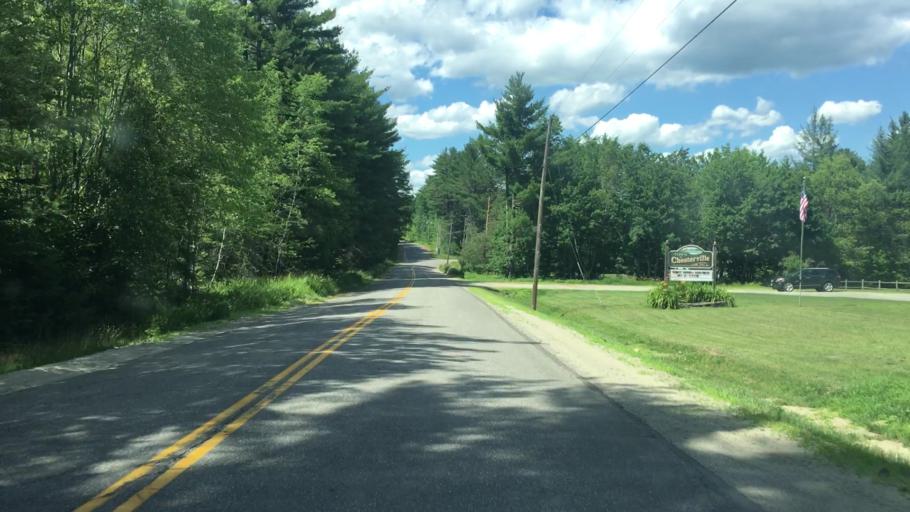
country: US
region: Maine
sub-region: Franklin County
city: Chesterville
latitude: 44.5786
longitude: -70.0904
